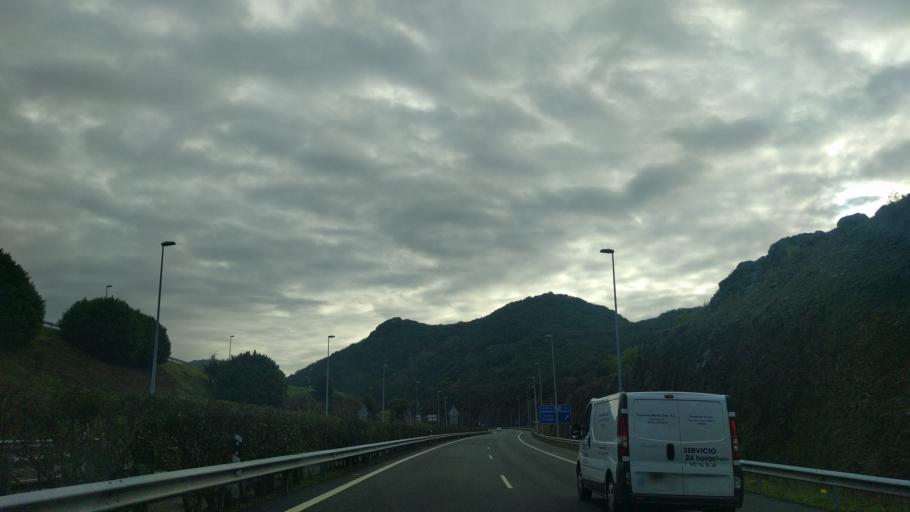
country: ES
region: Cantabria
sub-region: Provincia de Cantabria
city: Liendo
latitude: 43.3902
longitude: -3.3508
